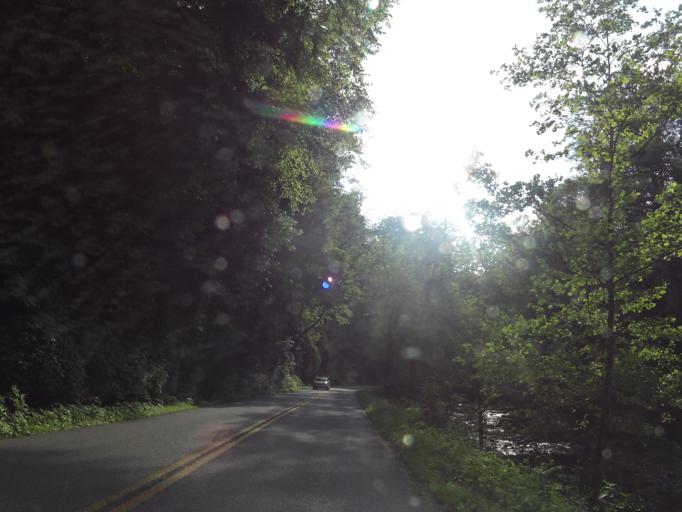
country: US
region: Tennessee
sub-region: Sevier County
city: Pigeon Forge
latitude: 35.6662
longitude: -83.6824
